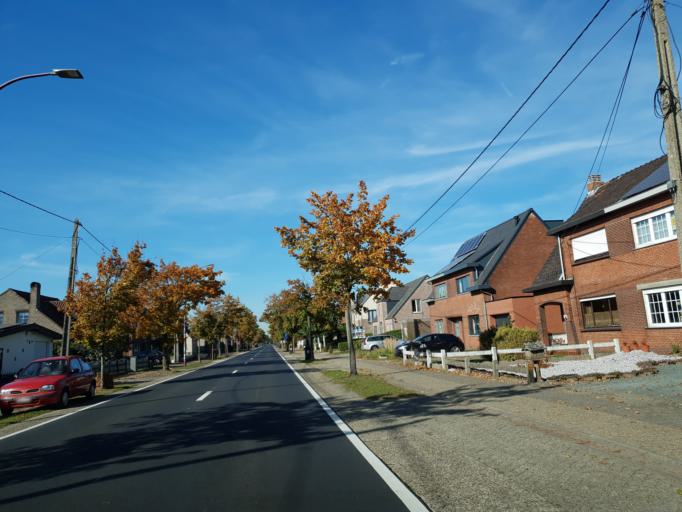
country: BE
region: Flanders
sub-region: Provincie Antwerpen
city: Stabroek
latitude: 51.3216
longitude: 4.3890
